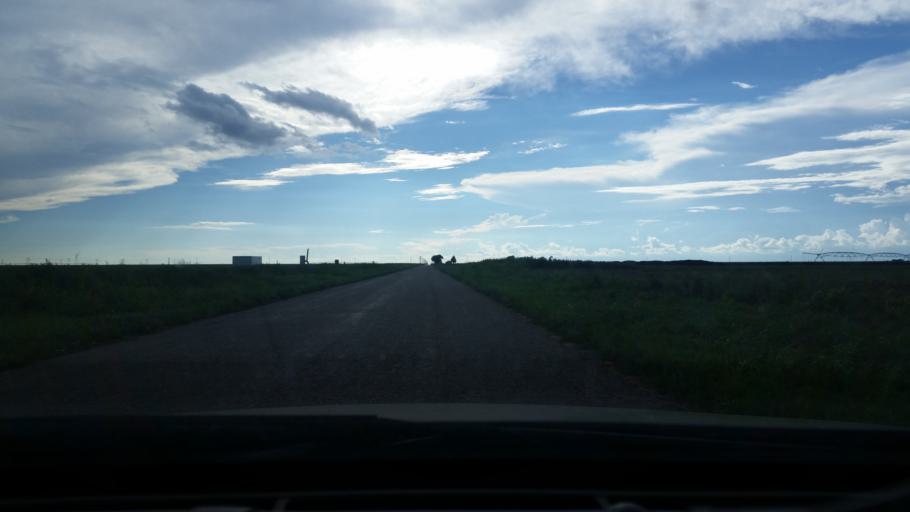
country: US
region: New Mexico
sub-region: Curry County
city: Clovis
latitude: 34.4630
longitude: -103.2216
